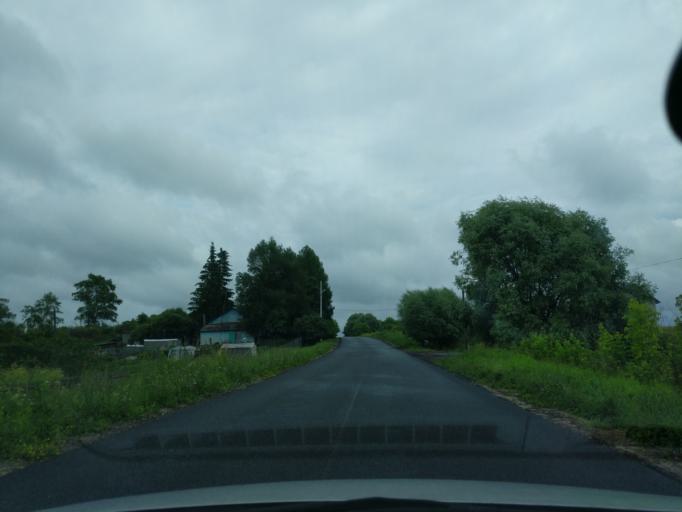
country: RU
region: Kaluga
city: Myatlevo
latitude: 54.7997
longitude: 35.7338
